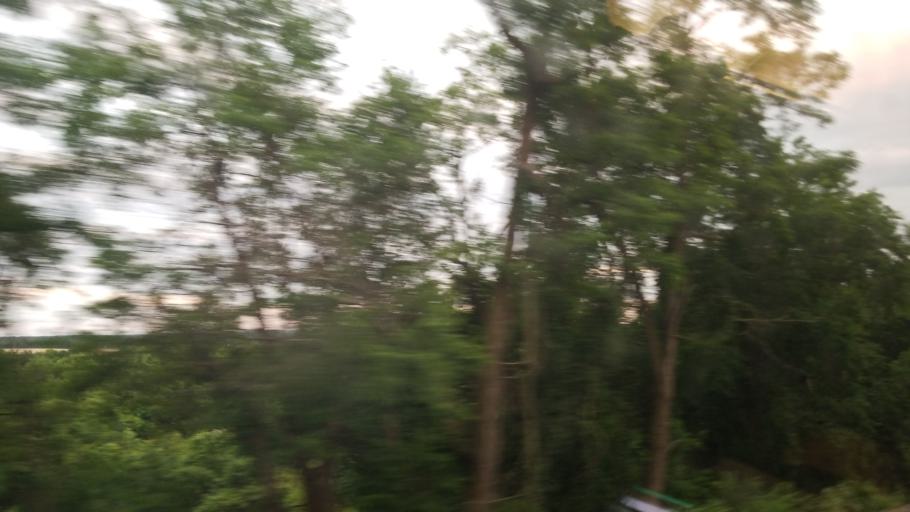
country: US
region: Virginia
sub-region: Culpeper County
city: Culpeper
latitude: 38.4366
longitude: -77.9943
